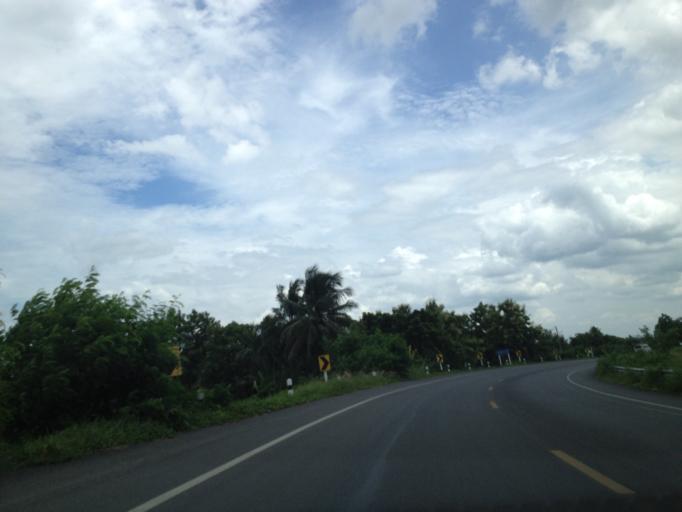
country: TH
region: Chiang Mai
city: San Pa Tong
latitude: 18.6339
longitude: 98.8753
